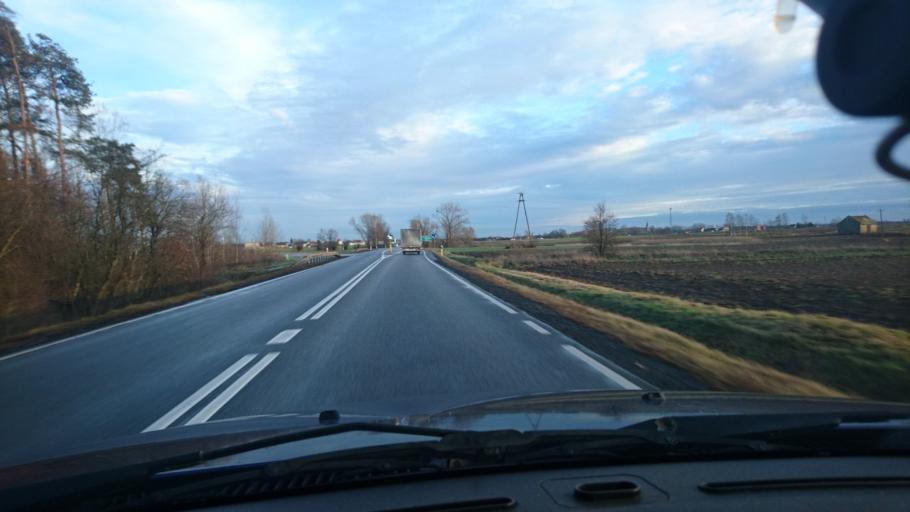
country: PL
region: Greater Poland Voivodeship
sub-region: Powiat kepinski
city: Opatow
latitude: 51.2218
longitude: 18.1266
